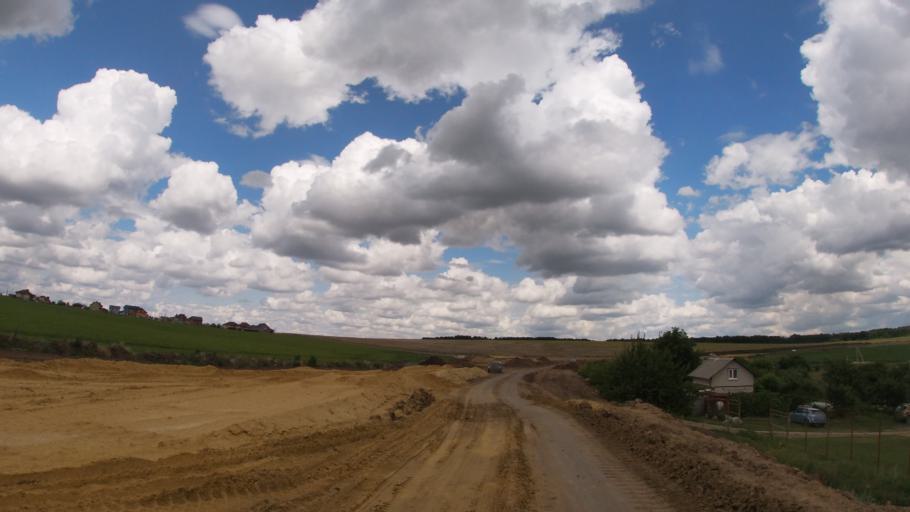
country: RU
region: Belgorod
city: Mayskiy
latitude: 50.5166
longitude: 36.4915
